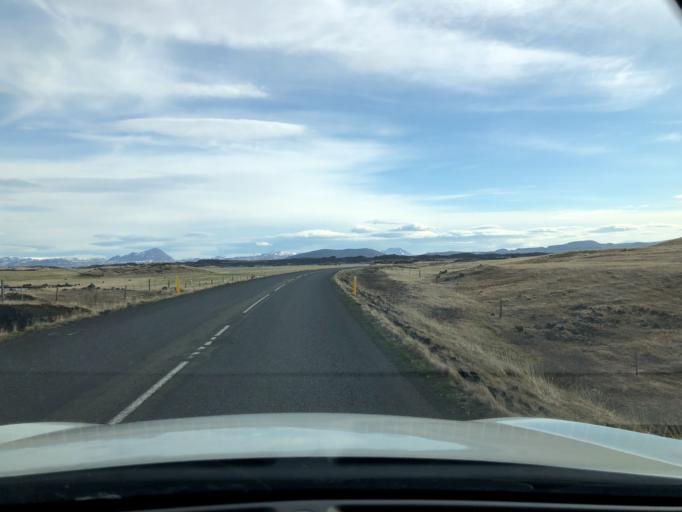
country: IS
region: Northeast
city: Laugar
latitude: 65.5547
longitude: -16.9644
